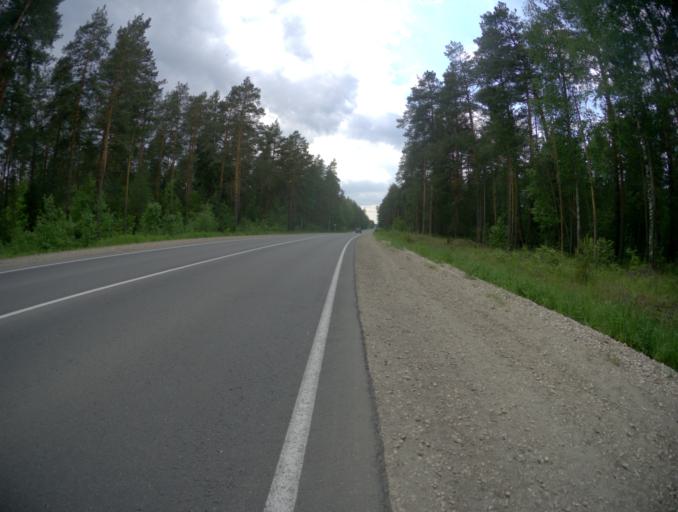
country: RU
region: Vladimir
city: Golovino
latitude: 56.0303
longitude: 40.4082
